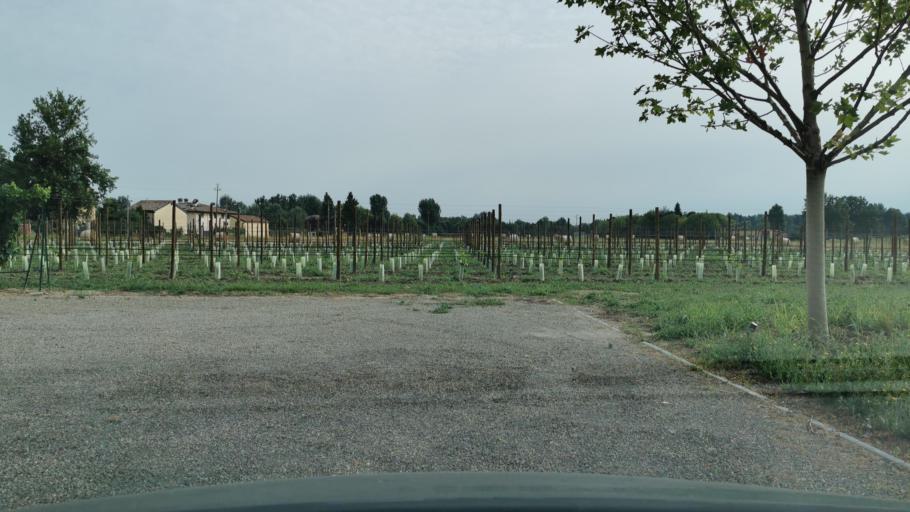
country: IT
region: Emilia-Romagna
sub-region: Provincia di Modena
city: Villanova
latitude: 44.6905
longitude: 10.9014
